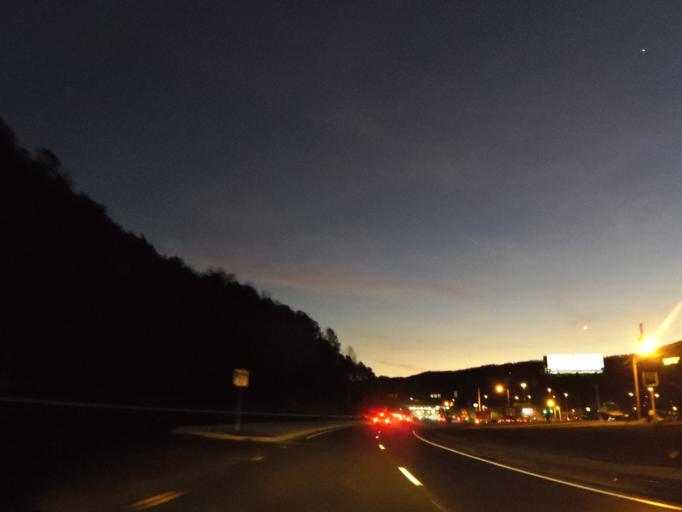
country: US
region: Georgia
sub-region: Whitfield County
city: Dalton
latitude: 34.7971
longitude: -84.9943
